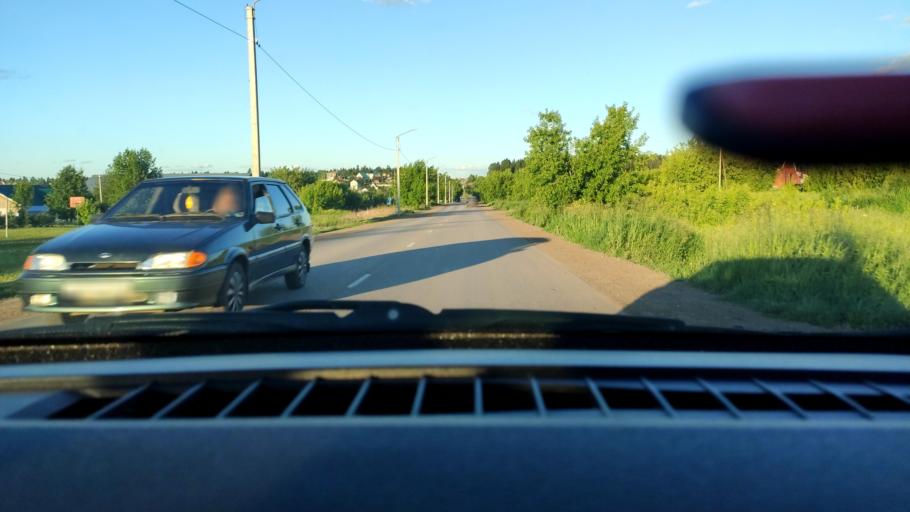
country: RU
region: Perm
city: Kultayevo
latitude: 57.9260
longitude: 55.8894
